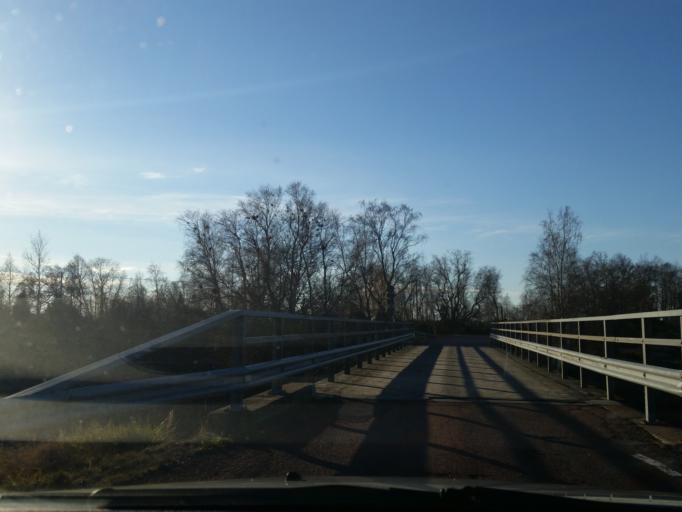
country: AX
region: Alands skaergard
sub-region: Braendoe
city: Braendoe
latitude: 60.4283
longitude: 21.0179
